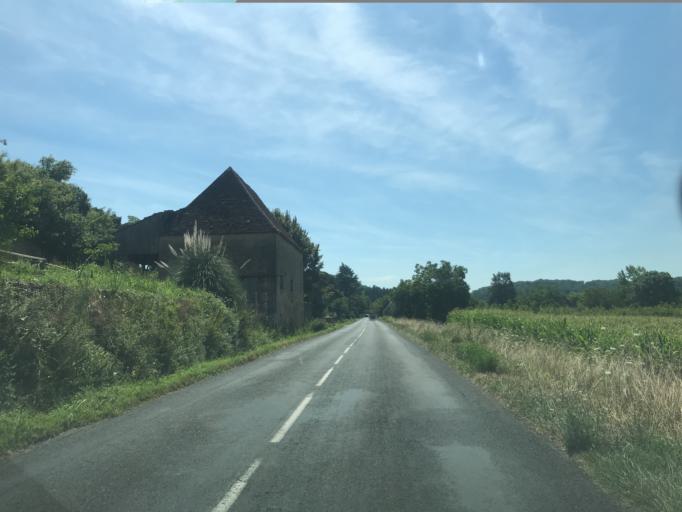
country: FR
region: Aquitaine
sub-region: Departement de la Dordogne
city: Cenac-et-Saint-Julien
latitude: 44.8152
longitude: 1.1943
